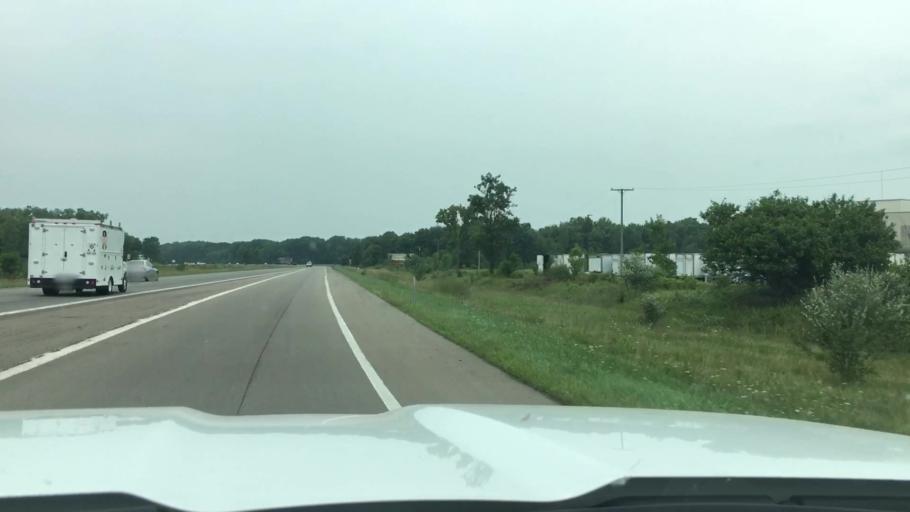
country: US
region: Michigan
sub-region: Ingham County
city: Webberville
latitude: 42.6619
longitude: -84.2028
